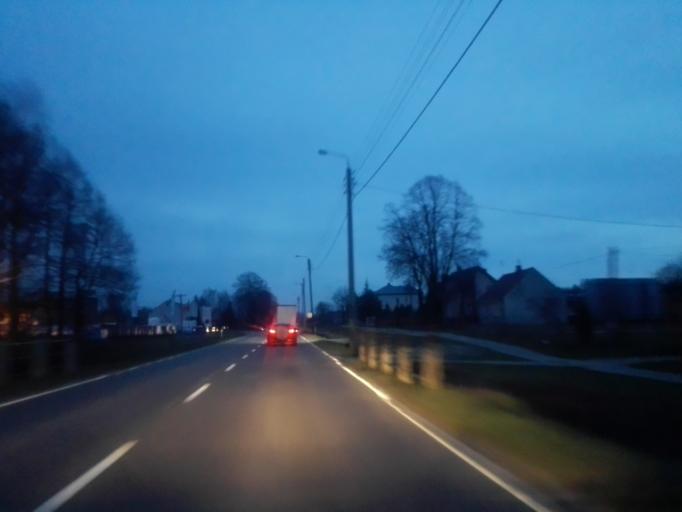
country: PL
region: Podlasie
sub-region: Lomza
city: Lomza
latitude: 53.1433
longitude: 22.0450
